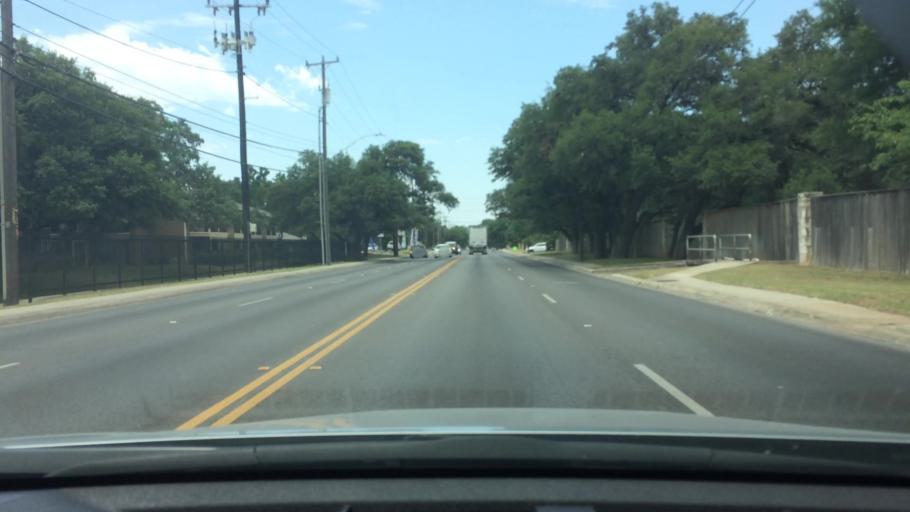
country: US
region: Texas
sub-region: Bexar County
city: Hollywood Park
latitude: 29.5740
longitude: -98.4463
